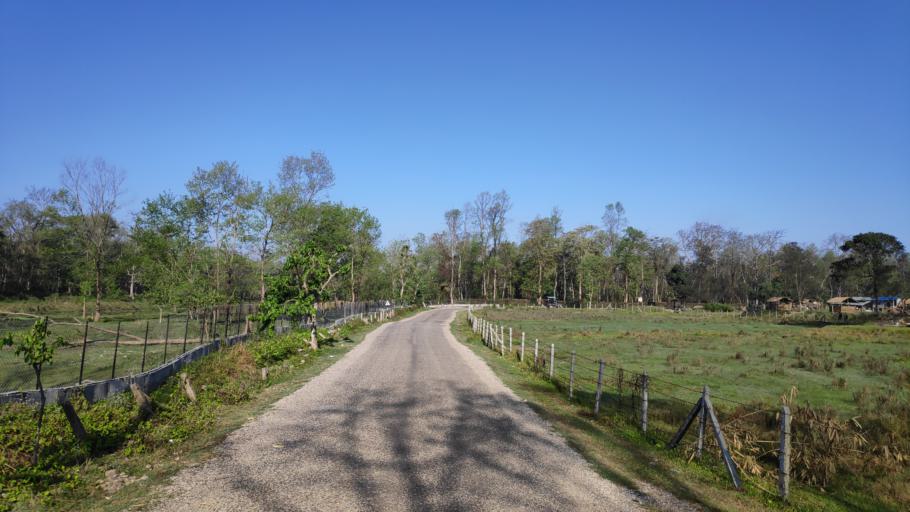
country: NP
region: Central Region
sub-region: Narayani Zone
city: Bharatpur
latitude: 27.5693
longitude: 84.5186
